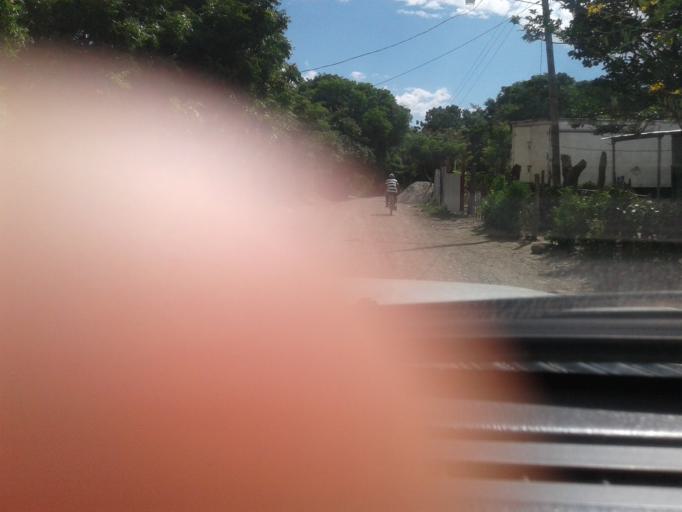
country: NI
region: Matagalpa
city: Ciudad Dario
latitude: 12.8458
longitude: -86.1213
